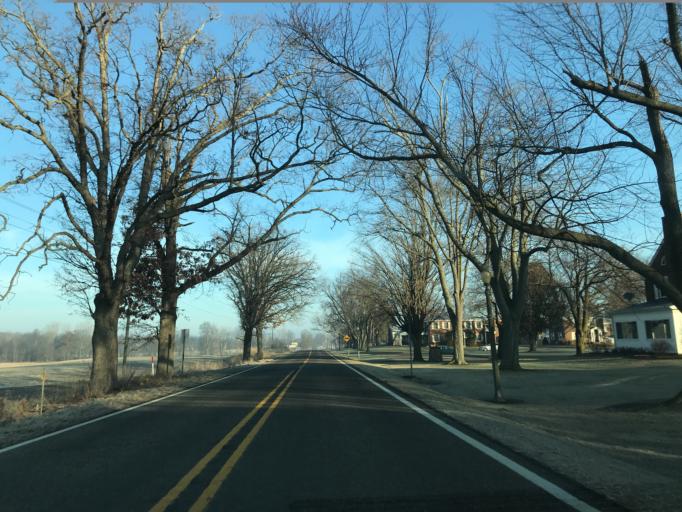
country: US
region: Michigan
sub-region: Eaton County
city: Eaton Rapids
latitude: 42.4762
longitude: -84.6009
